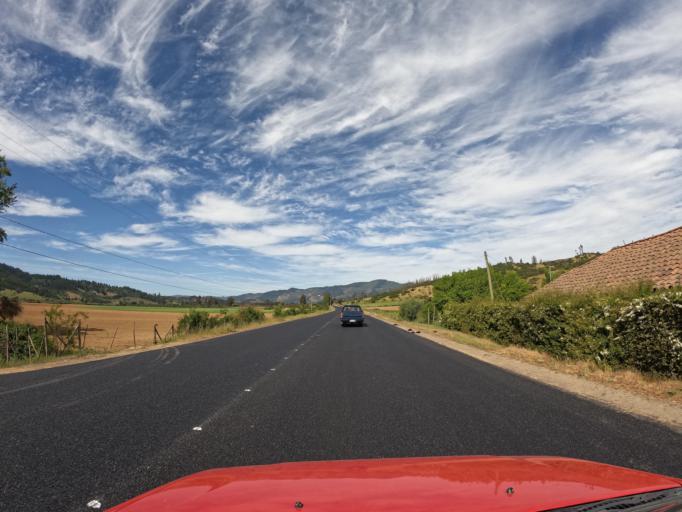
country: CL
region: Maule
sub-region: Provincia de Talca
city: Talca
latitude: -35.0993
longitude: -71.9987
